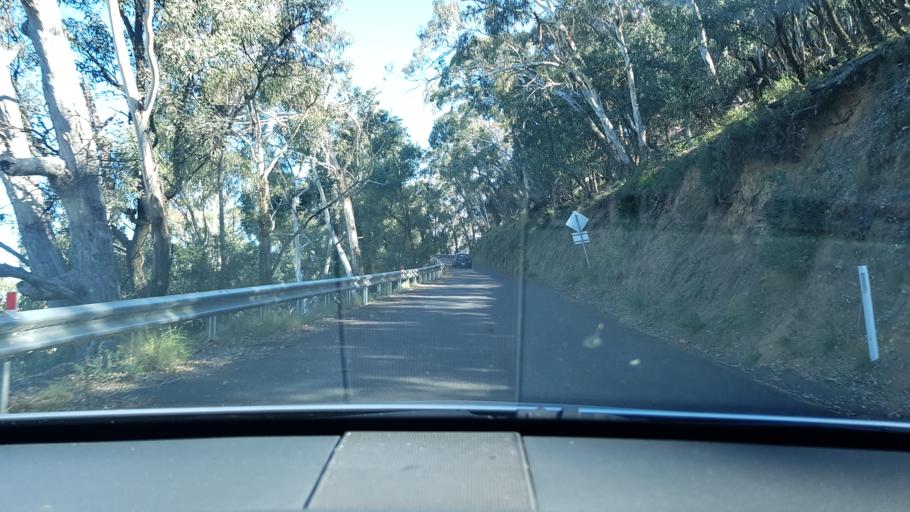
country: AU
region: New South Wales
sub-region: Oberon
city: Oberon
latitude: -33.8150
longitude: 150.0178
